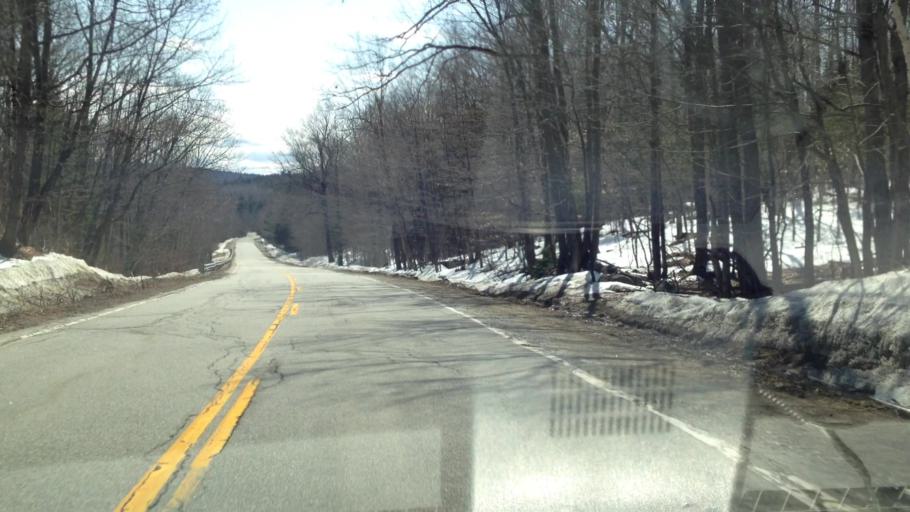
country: US
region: New Hampshire
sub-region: Sullivan County
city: Springfield
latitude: 43.4865
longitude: -71.9784
